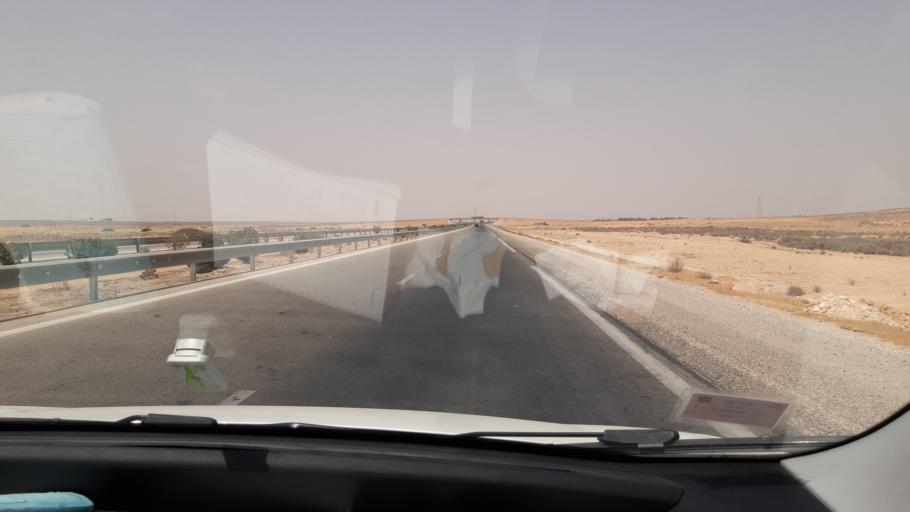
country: TN
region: Qabis
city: Gabes
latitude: 33.9057
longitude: 9.9760
